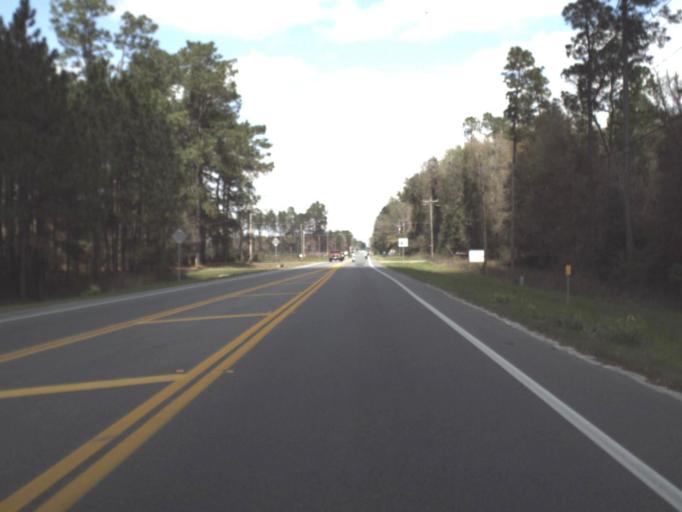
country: US
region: Florida
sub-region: Wakulla County
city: Crawfordville
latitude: 30.2258
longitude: -84.3624
